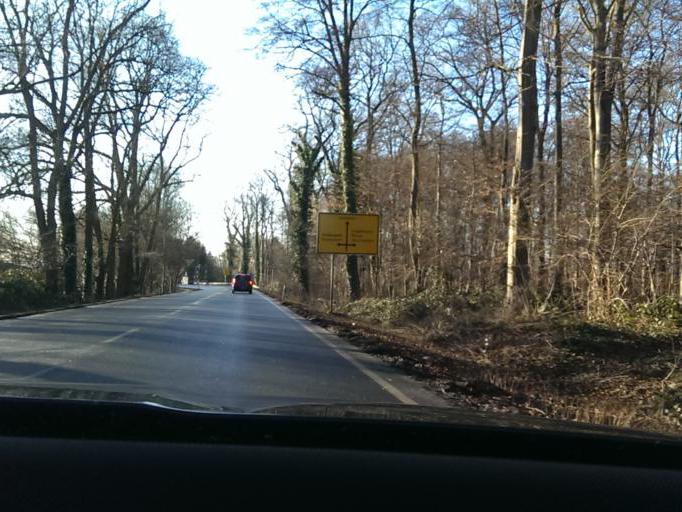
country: DE
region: Lower Saxony
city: Elze
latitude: 52.5236
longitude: 9.7252
